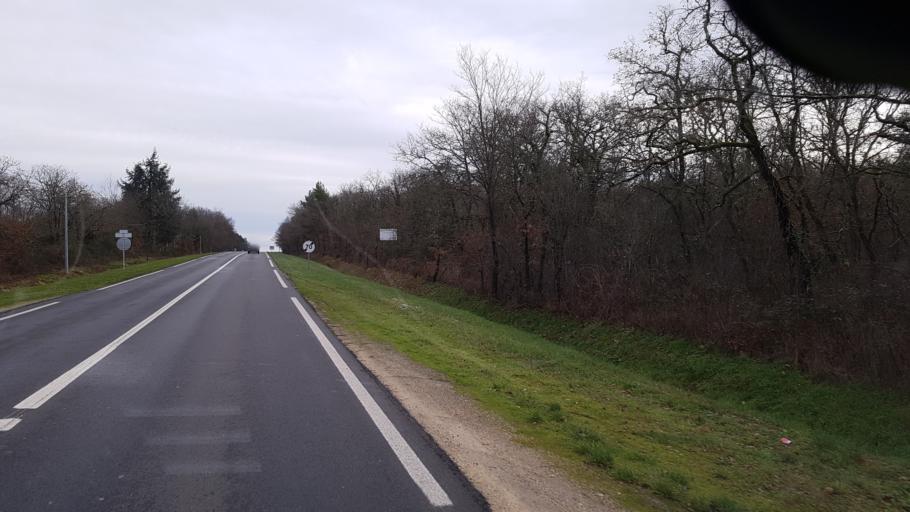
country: FR
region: Centre
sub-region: Departement du Loiret
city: Menestreau-en-Villette
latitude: 47.6500
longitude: 1.9896
